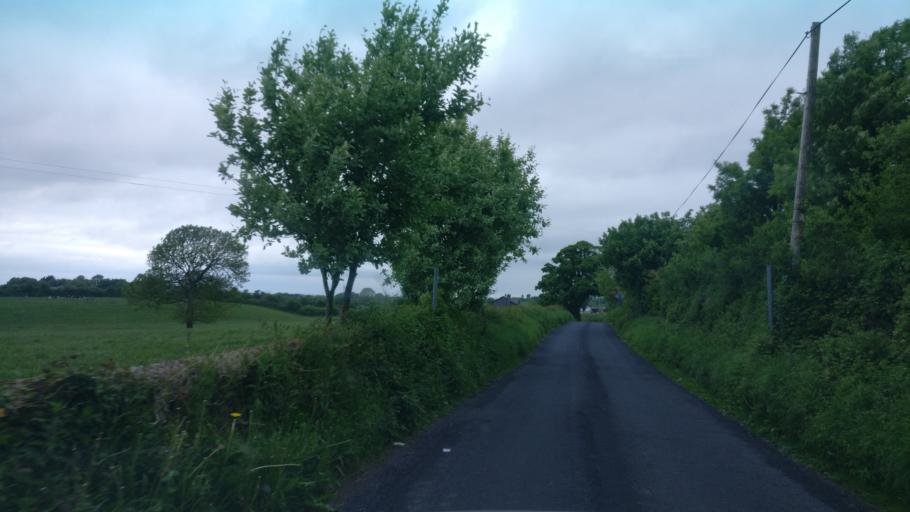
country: IE
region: Connaught
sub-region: County Galway
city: Portumna
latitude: 53.1128
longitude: -8.2874
